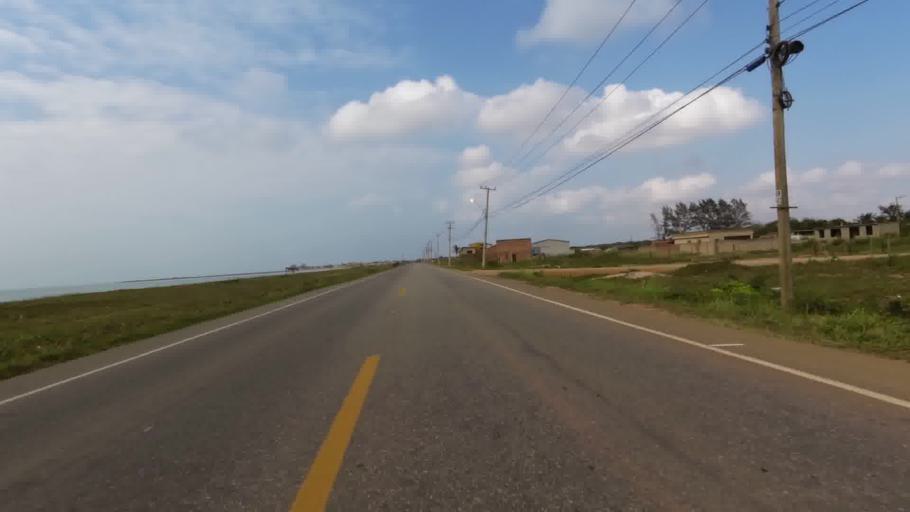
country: BR
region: Espirito Santo
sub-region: Itapemirim
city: Itapemirim
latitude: -20.9864
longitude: -40.8116
